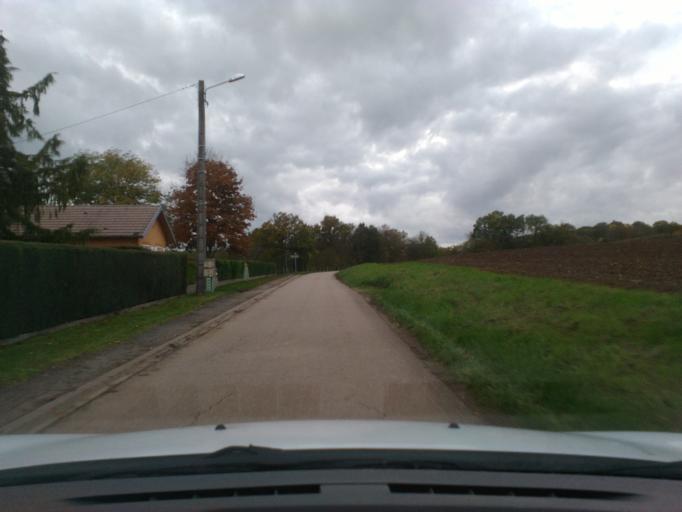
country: FR
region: Lorraine
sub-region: Departement des Vosges
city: Mirecourt
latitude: 48.3412
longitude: 6.1354
